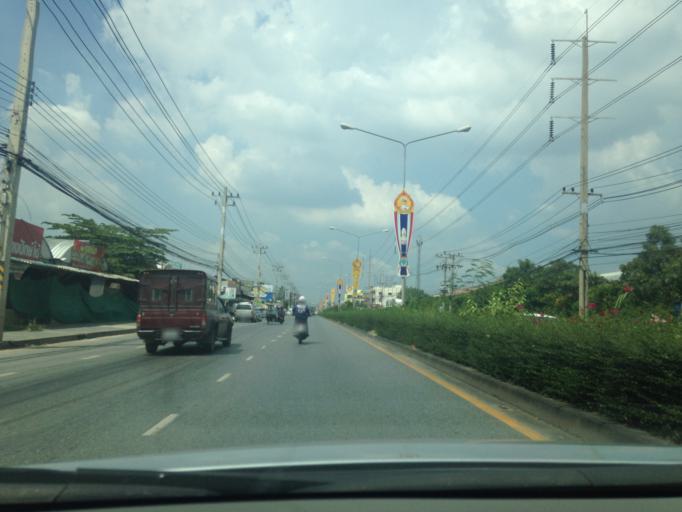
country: TH
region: Pathum Thani
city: Pathum Thani
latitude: 14.0360
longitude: 100.5252
